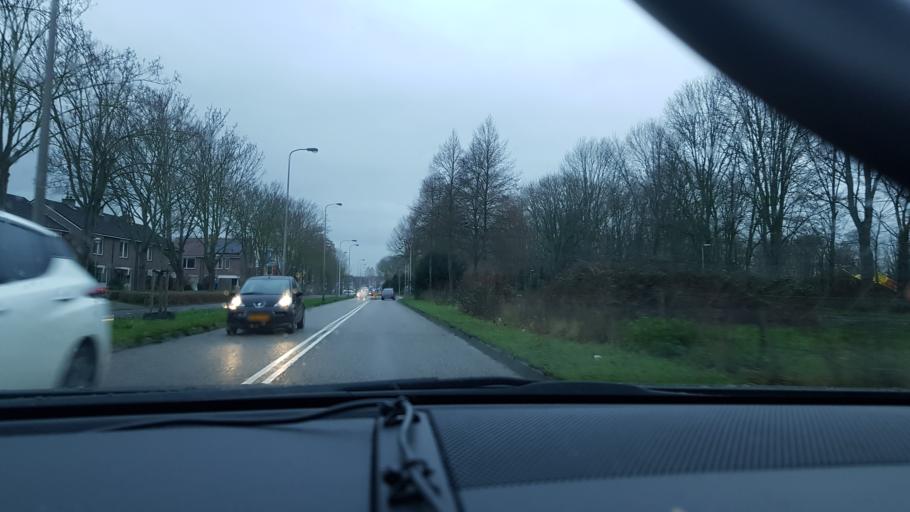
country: NL
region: Limburg
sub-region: Gemeente Roermond
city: Leeuwen
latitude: 51.1922
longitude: 6.0103
